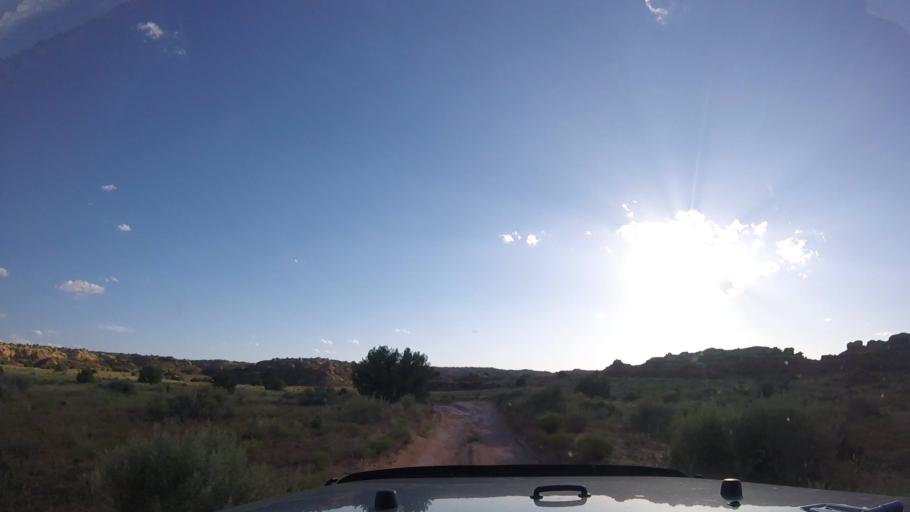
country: US
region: Utah
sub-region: Grand County
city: Moab
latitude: 38.1966
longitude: -109.7824
